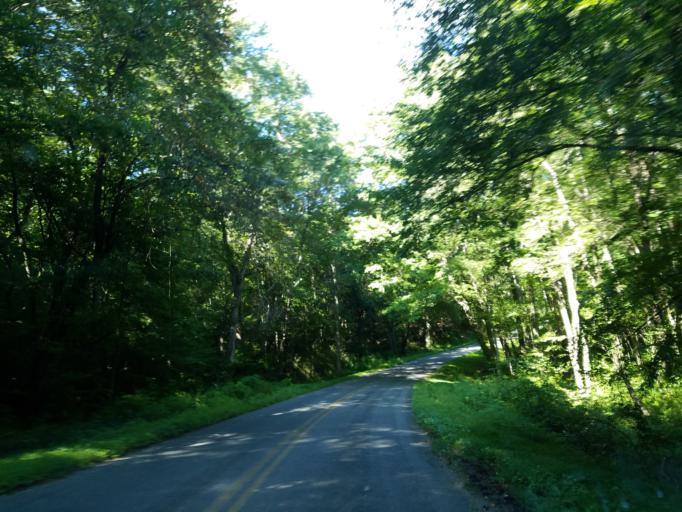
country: US
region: Georgia
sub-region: Gilmer County
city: Ellijay
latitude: 34.6376
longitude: -84.3587
